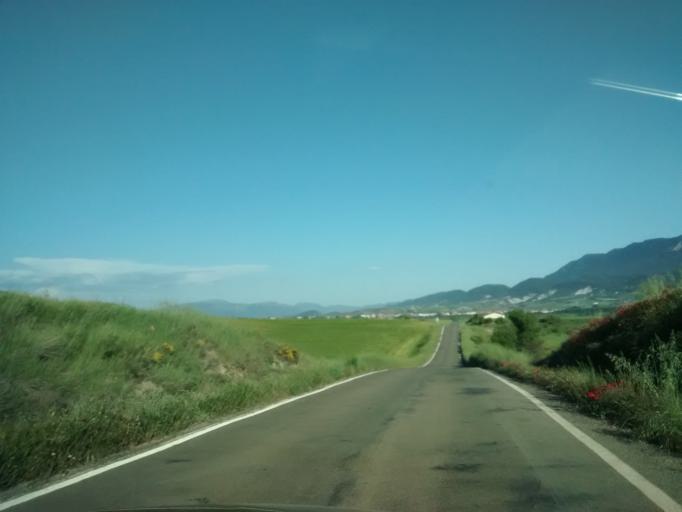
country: ES
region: Aragon
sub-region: Provincia de Huesca
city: Jaca
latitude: 42.5865
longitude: -0.6035
